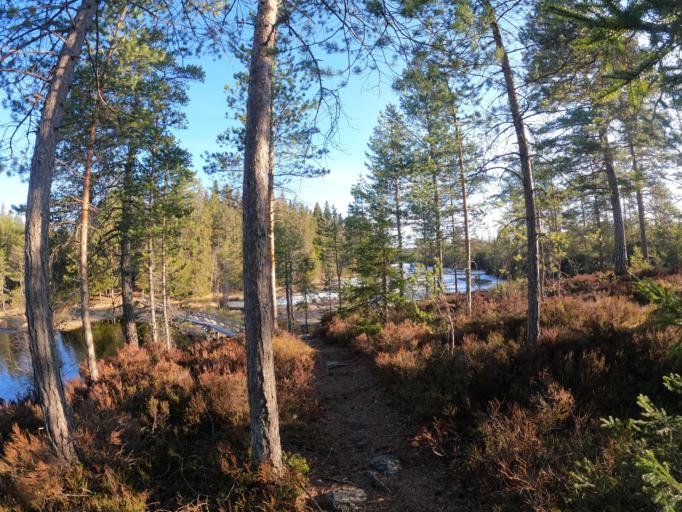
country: NO
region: Akershus
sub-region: Nittedal
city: Aneby
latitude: 60.1308
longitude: 10.9120
